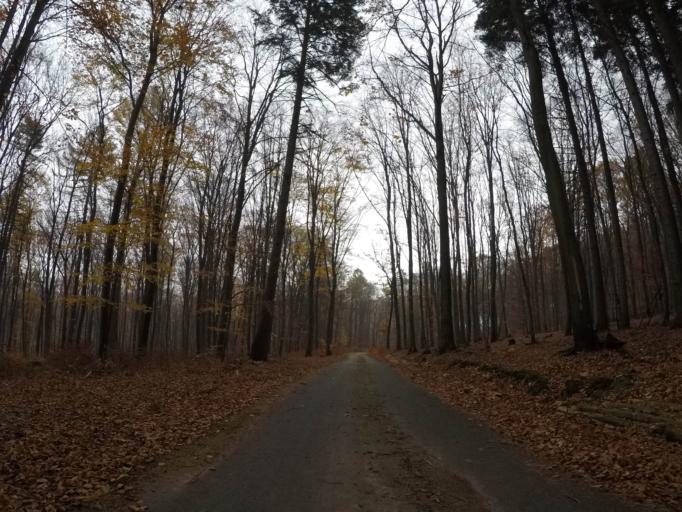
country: SK
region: Presovsky
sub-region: Okres Presov
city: Presov
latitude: 48.8855
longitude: 21.1918
